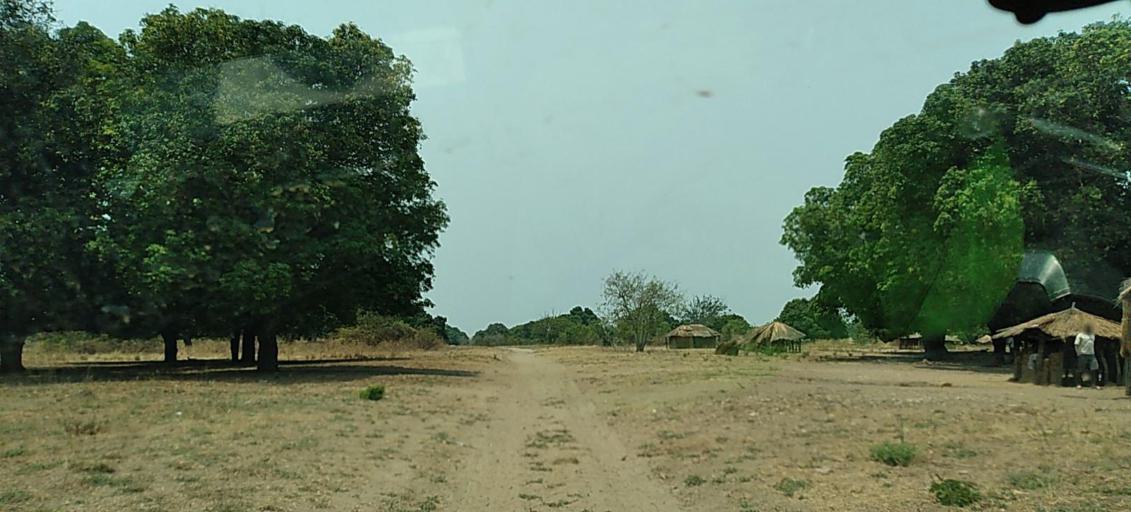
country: ZM
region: Western
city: Lukulu
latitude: -14.1564
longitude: 23.3064
